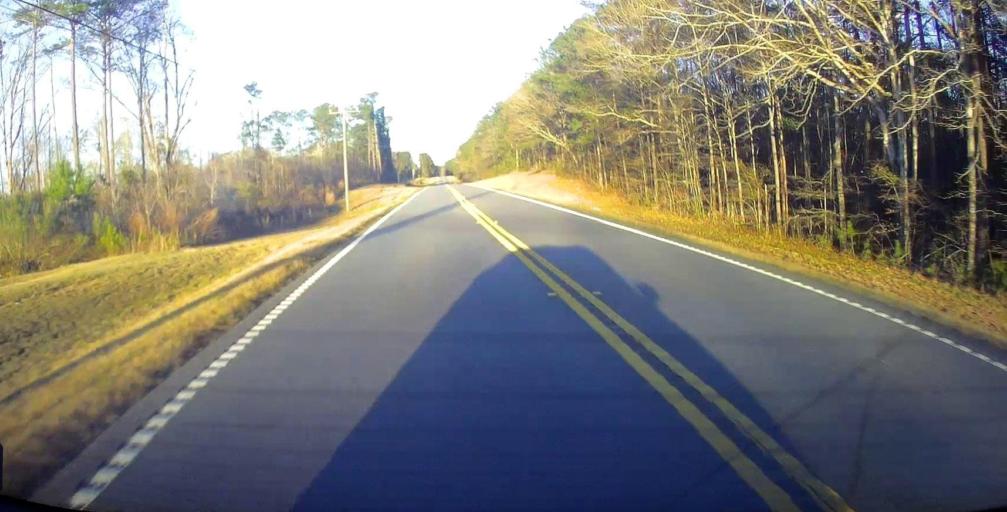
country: US
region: Georgia
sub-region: Harris County
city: Hamilton
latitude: 32.6585
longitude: -84.9939
